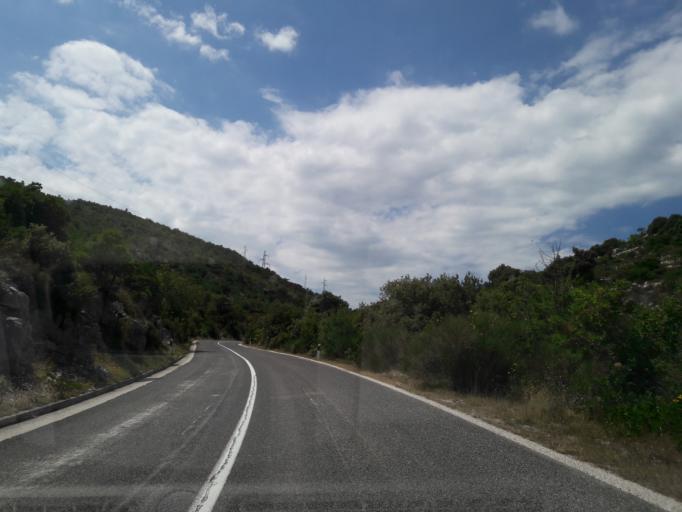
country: HR
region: Dubrovacko-Neretvanska
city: Orebic
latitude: 42.9695
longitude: 17.2825
